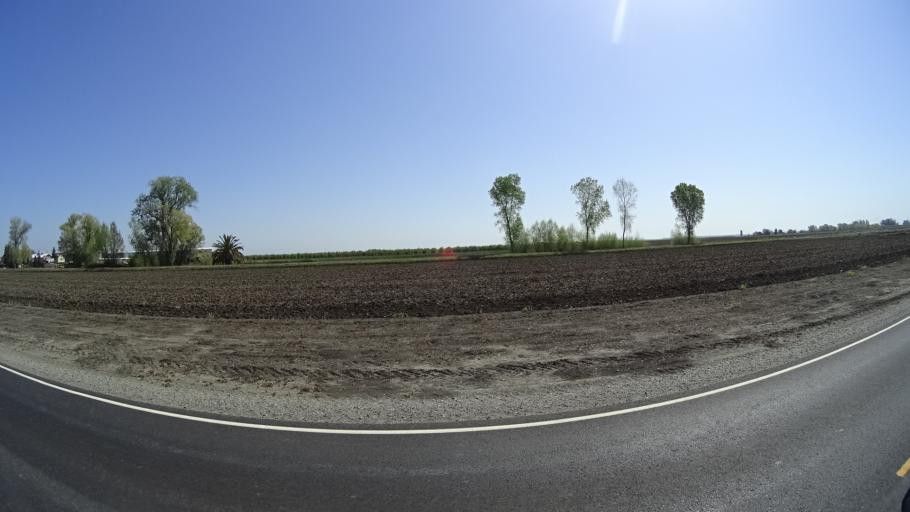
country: US
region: California
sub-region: Glenn County
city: Hamilton City
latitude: 39.6135
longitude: -122.0653
